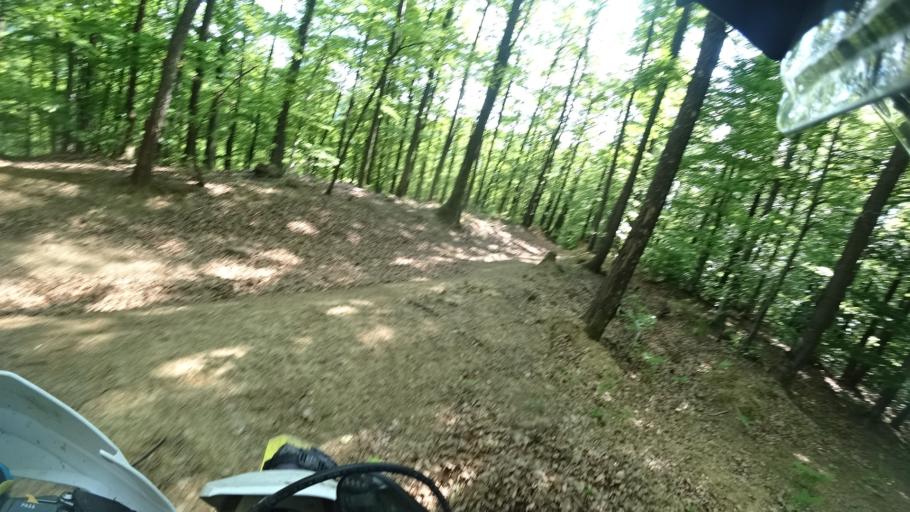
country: HR
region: Zagrebacka
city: Jablanovec
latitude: 45.8960
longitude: 15.8998
